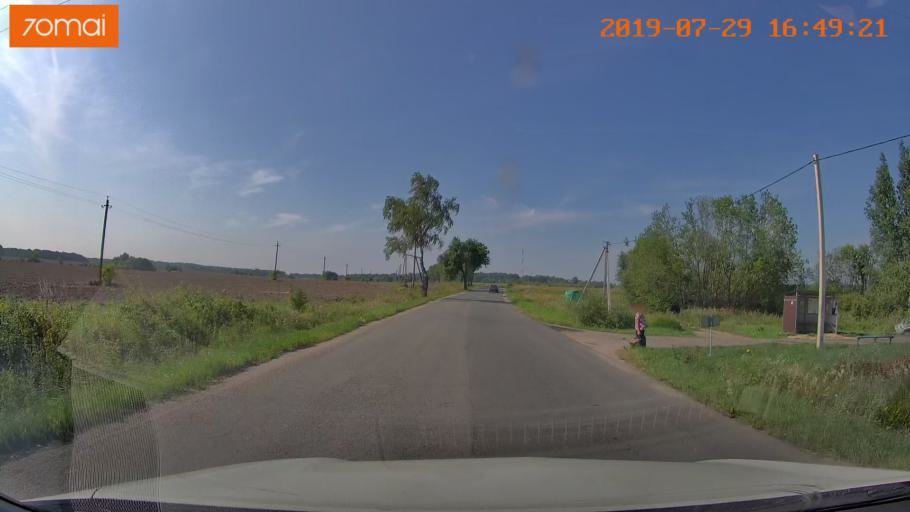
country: RU
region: Kaliningrad
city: Primorsk
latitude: 54.7933
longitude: 20.0661
